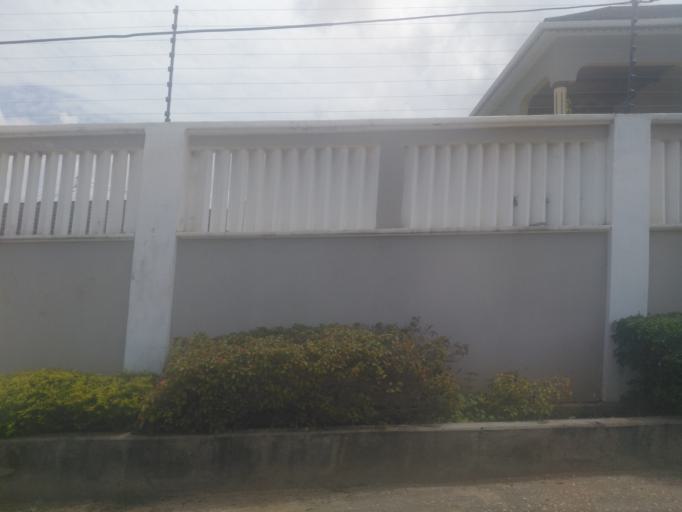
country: TZ
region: Zanzibar Urban/West
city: Zanzibar
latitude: -6.2384
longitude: 39.2140
